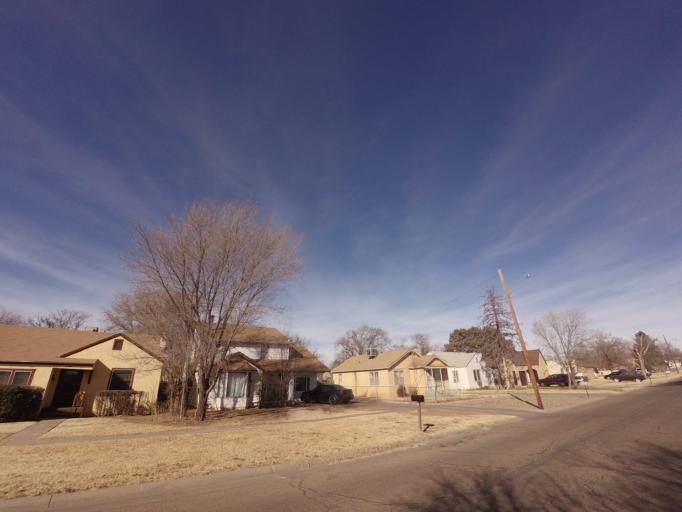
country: US
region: New Mexico
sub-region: Curry County
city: Clovis
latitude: 34.4130
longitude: -103.1990
